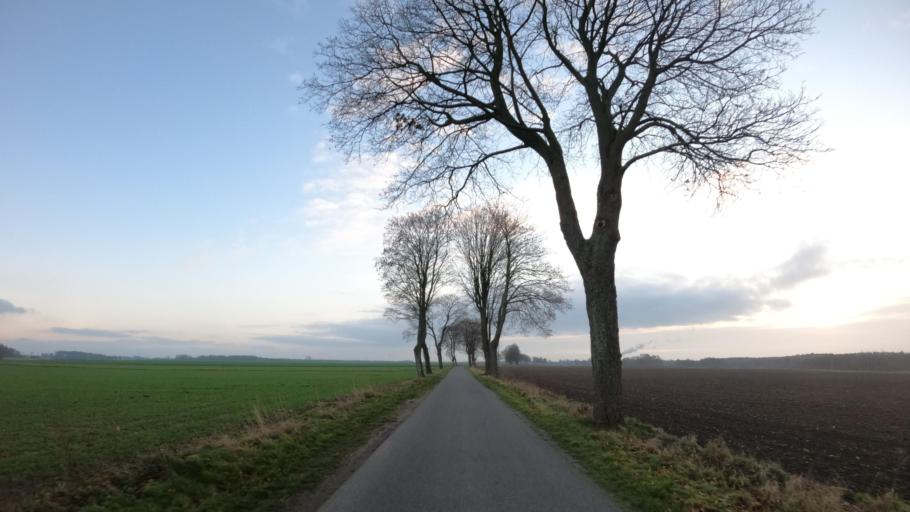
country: PL
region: West Pomeranian Voivodeship
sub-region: Powiat bialogardzki
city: Karlino
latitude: 54.0953
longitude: 15.8862
